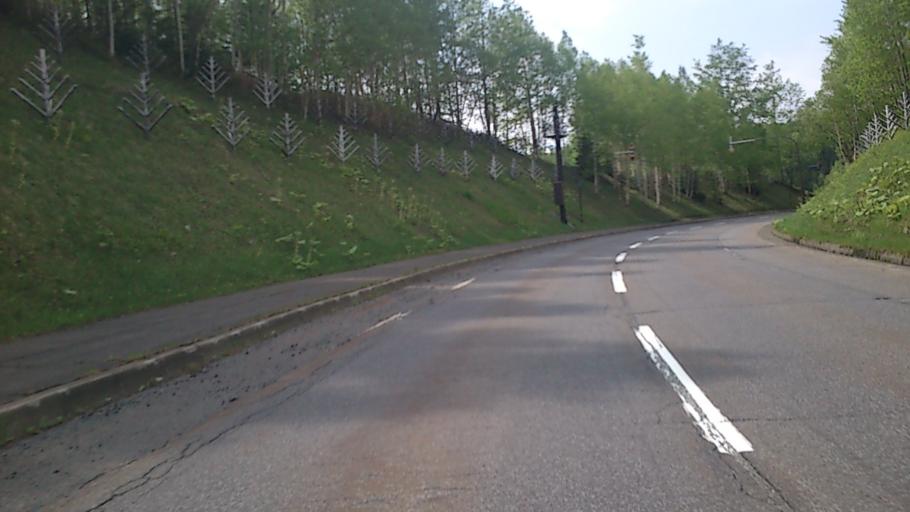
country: JP
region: Hokkaido
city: Kamikawa
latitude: 43.6676
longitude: 143.0373
